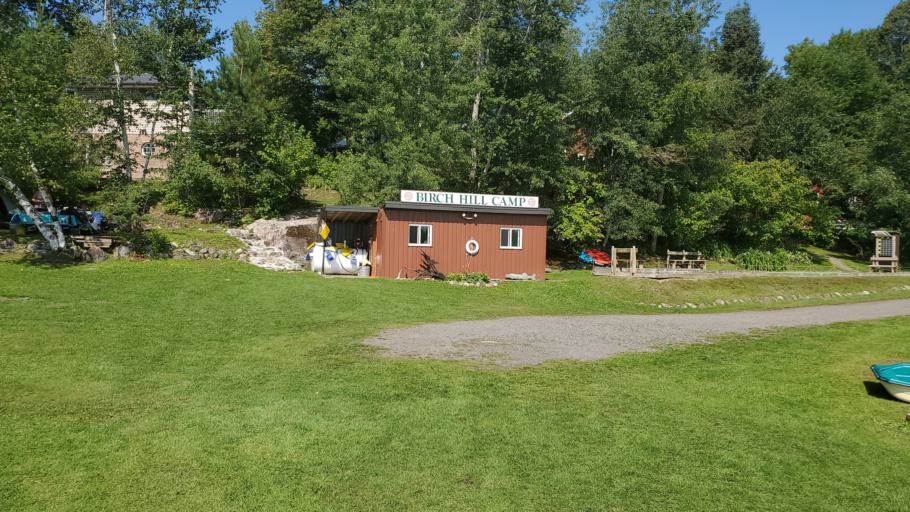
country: CA
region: Ontario
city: Powassan
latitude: 46.2260
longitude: -79.2278
